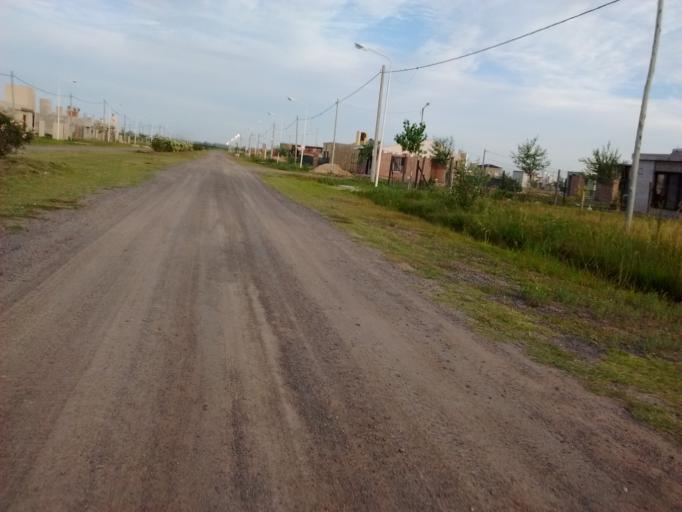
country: AR
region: Santa Fe
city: Roldan
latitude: -32.9380
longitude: -60.8796
